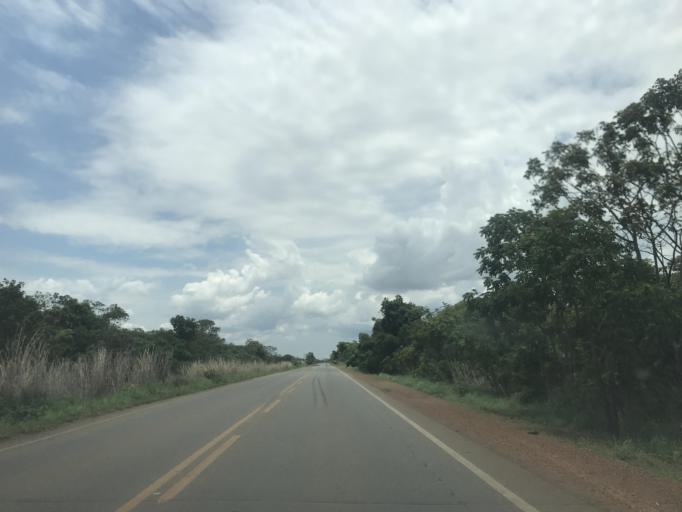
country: BR
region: Goias
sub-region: Vianopolis
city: Vianopolis
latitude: -16.7343
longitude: -48.4458
